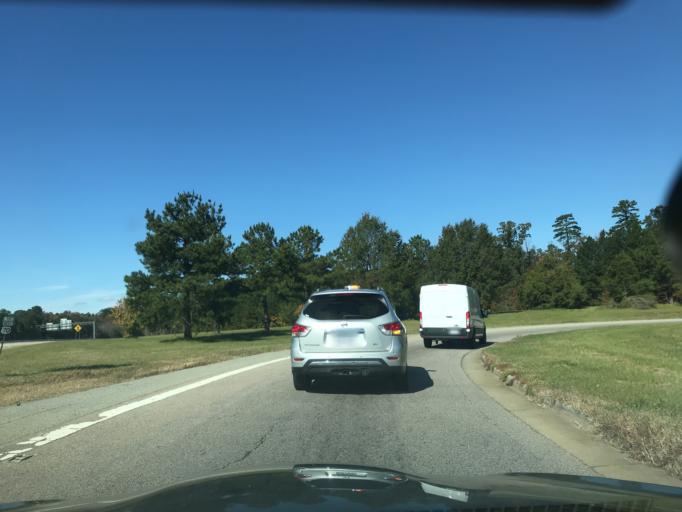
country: US
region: North Carolina
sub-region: Durham County
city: Durham
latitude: 36.0174
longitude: -78.9524
